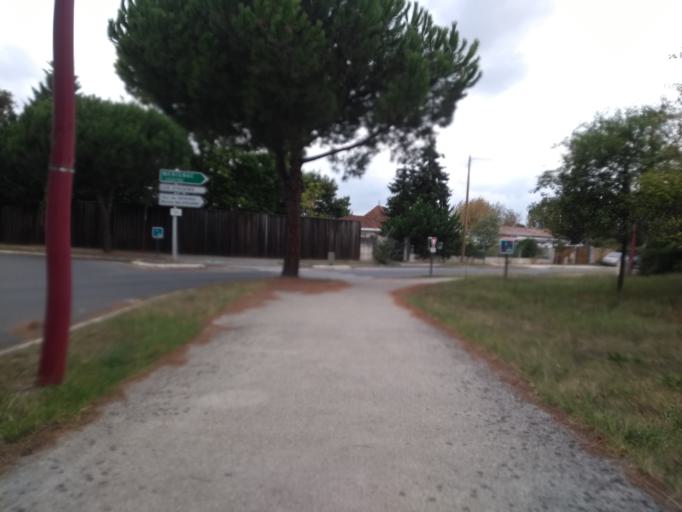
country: FR
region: Aquitaine
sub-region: Departement de la Gironde
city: Pessac
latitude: 44.8203
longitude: -0.6493
